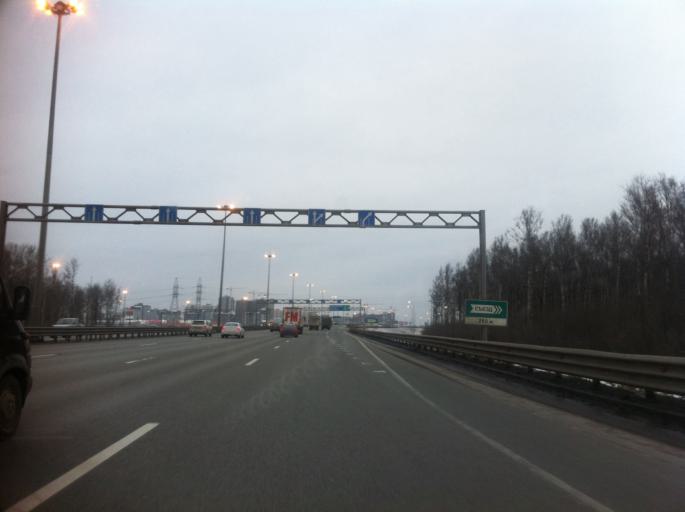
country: RU
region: Leningrad
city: Rybatskoye
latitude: 59.8786
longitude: 30.5294
